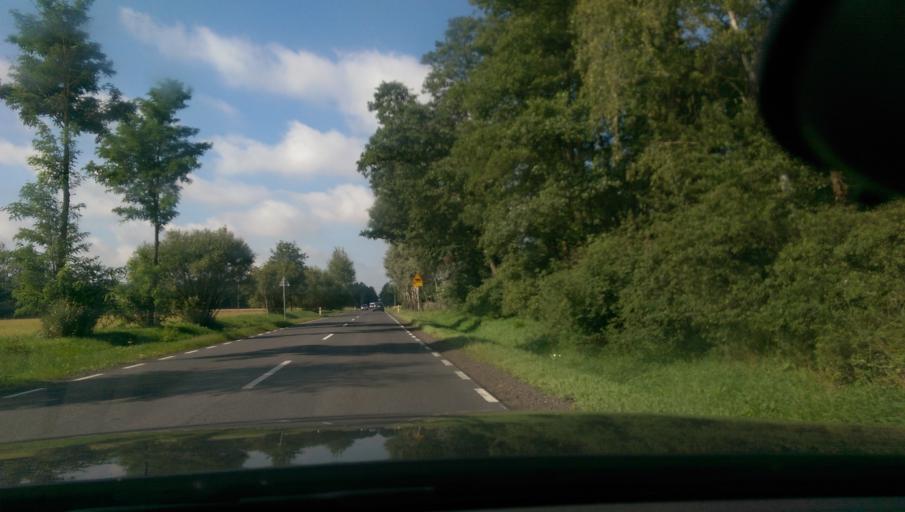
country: PL
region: Masovian Voivodeship
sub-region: Powiat plonski
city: Sochocin
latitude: 52.7158
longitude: 20.5004
